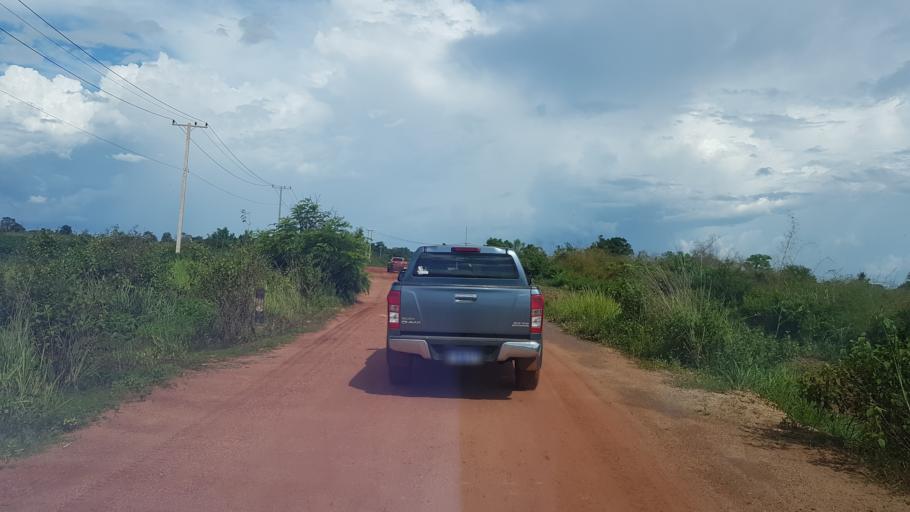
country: LA
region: Vientiane
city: Vientiane
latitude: 18.2085
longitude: 102.5662
